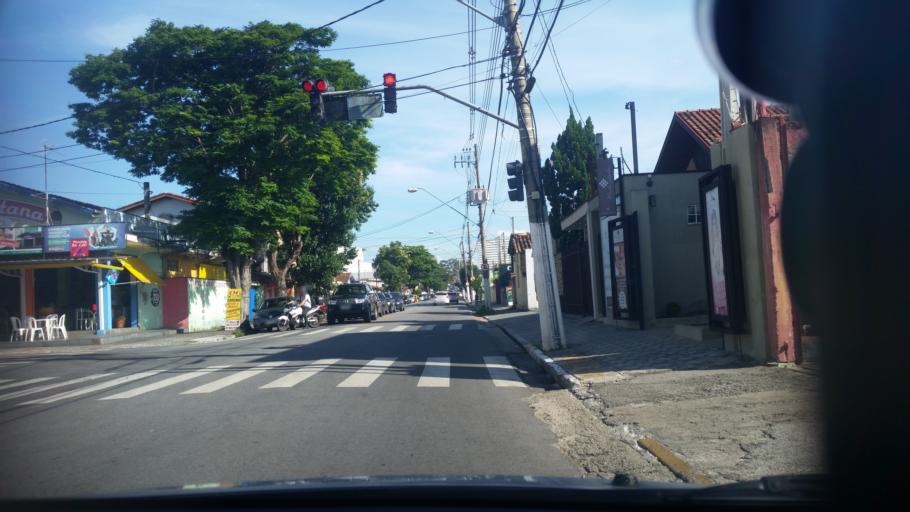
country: BR
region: Sao Paulo
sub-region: Taubate
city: Taubate
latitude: -23.0176
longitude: -45.5735
